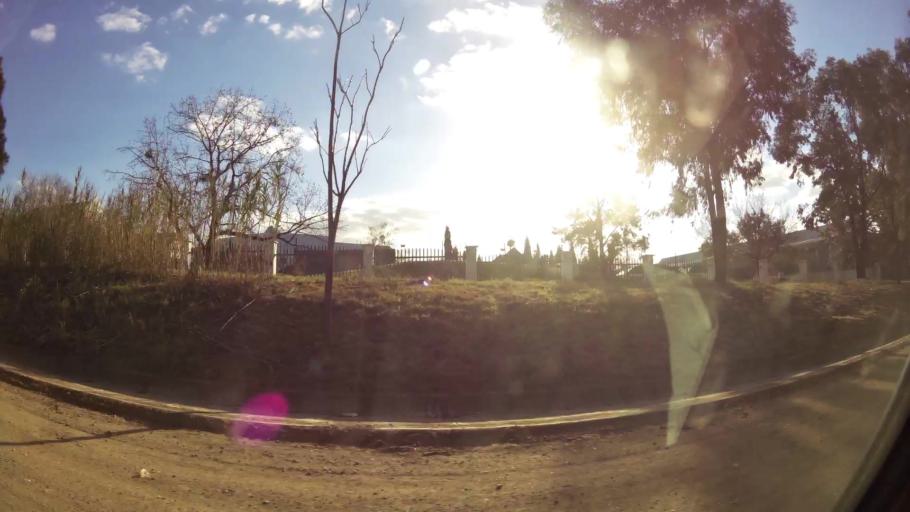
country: ZA
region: Gauteng
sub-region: City of Johannesburg Metropolitan Municipality
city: Midrand
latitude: -25.9704
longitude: 28.1364
